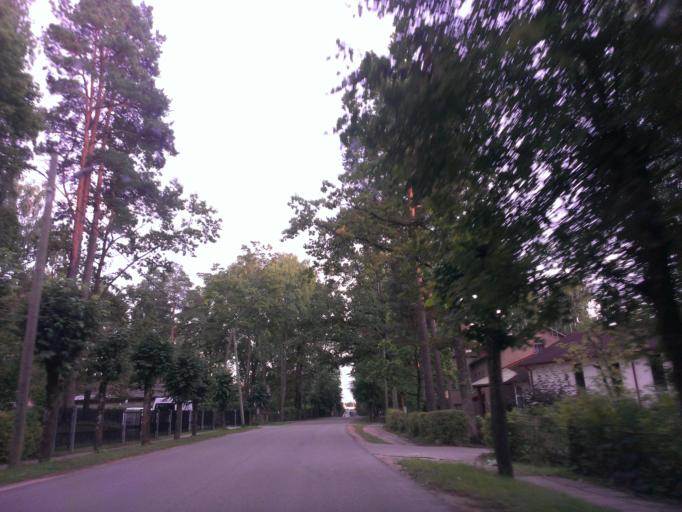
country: LV
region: Ogre
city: Ogre
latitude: 56.8226
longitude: 24.5879
